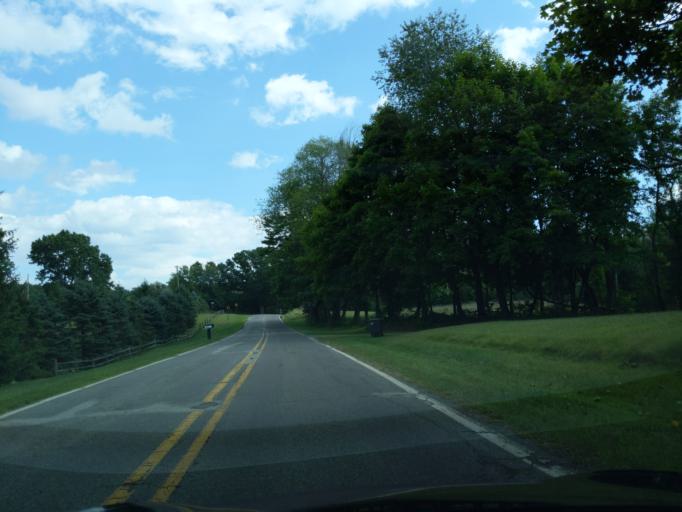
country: US
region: Michigan
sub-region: Jackson County
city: Spring Arbor
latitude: 42.3168
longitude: -84.5220
